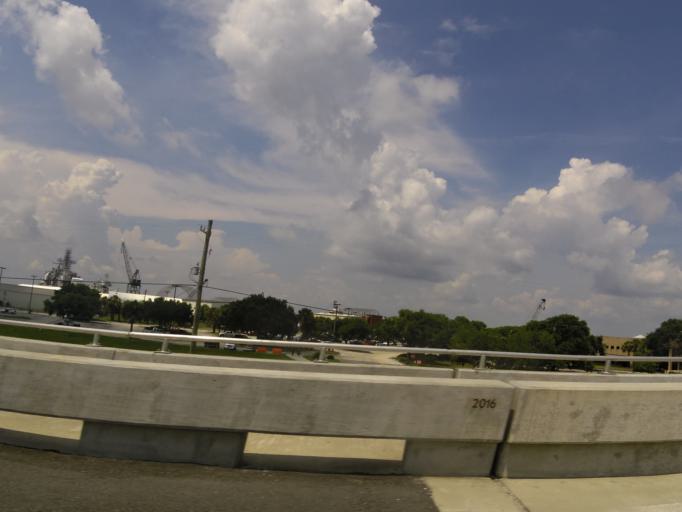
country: US
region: Florida
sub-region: Duval County
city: Atlantic Beach
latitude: 30.3904
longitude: -81.4568
